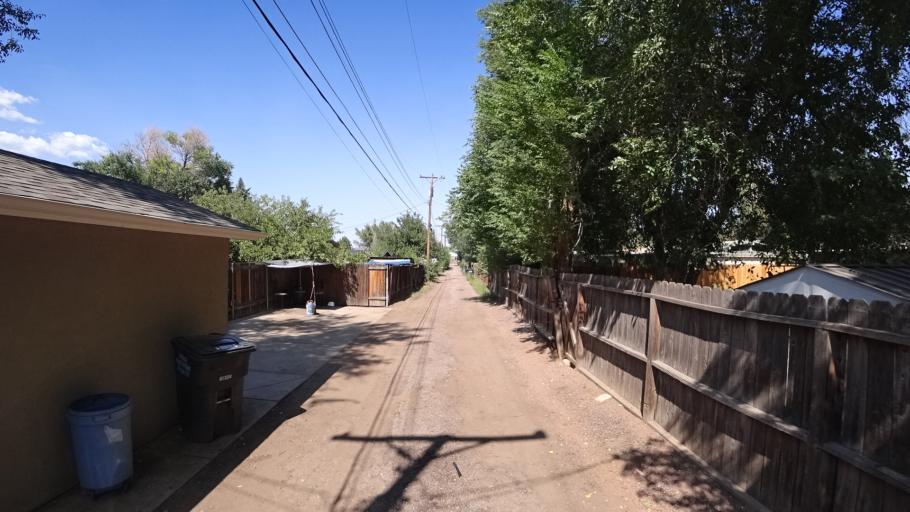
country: US
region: Colorado
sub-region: El Paso County
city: Colorado Springs
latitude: 38.8809
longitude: -104.8100
